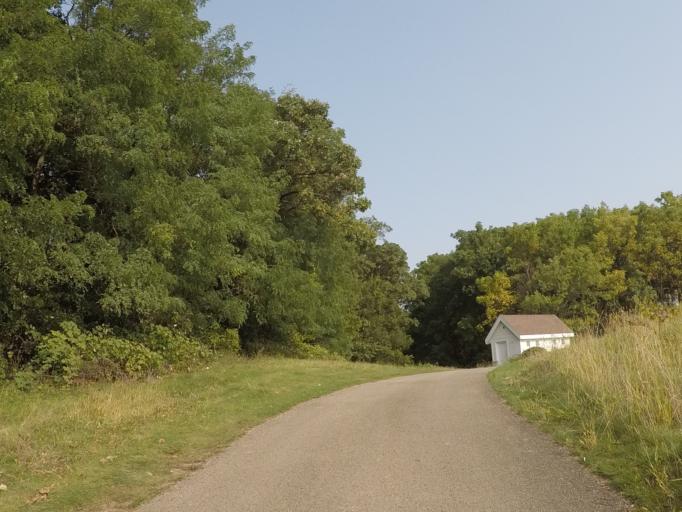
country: US
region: Wisconsin
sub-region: Dane County
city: Verona
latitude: 43.0375
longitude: -89.5377
